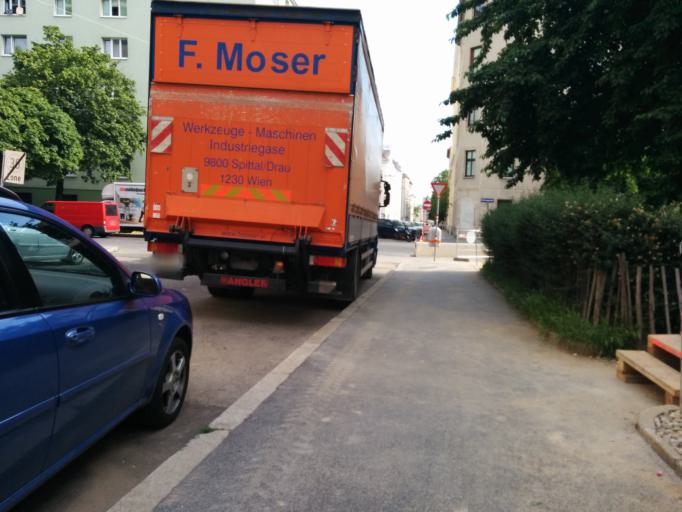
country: AT
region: Vienna
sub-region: Wien Stadt
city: Vienna
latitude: 48.1686
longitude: 16.3724
